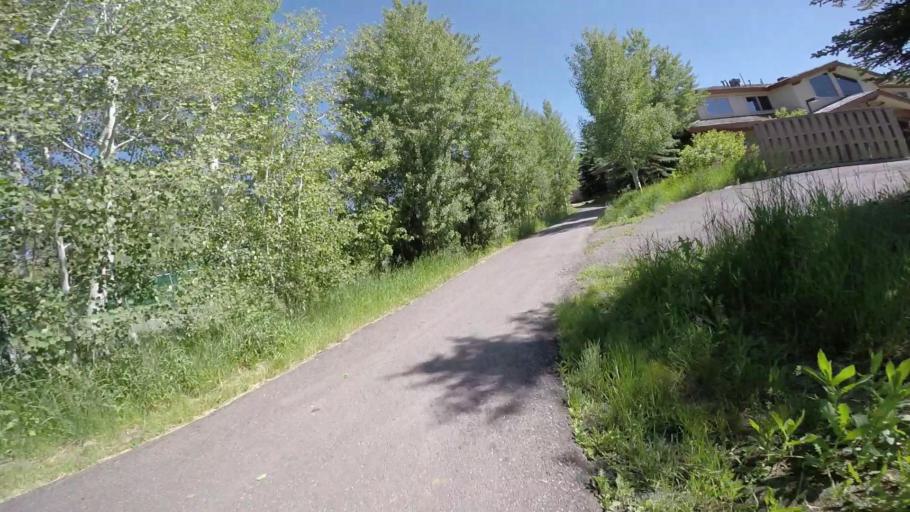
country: US
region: Utah
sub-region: Summit County
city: Park City
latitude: 40.6651
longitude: -111.5125
